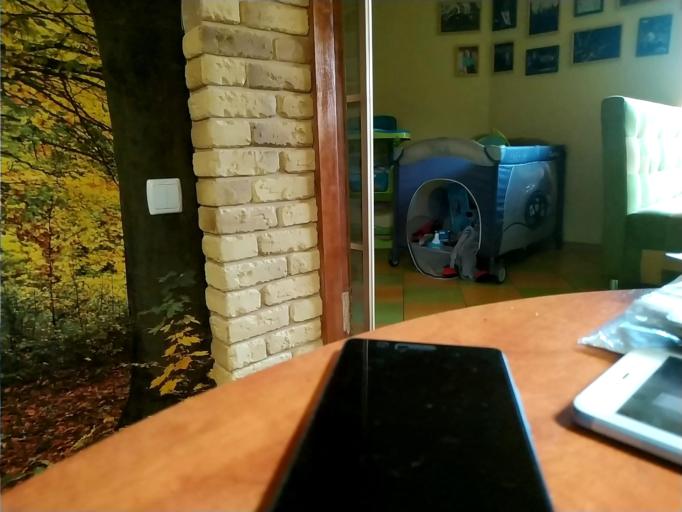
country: RU
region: Kaluga
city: Seredeyskiy
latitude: 53.7856
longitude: 35.3989
